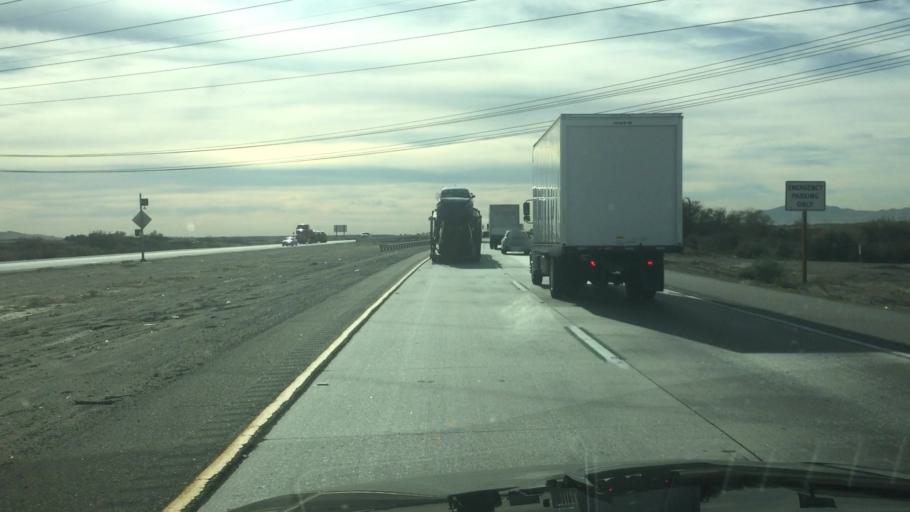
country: US
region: California
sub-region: Riverside County
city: Coachella
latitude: 33.6718
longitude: -116.1459
